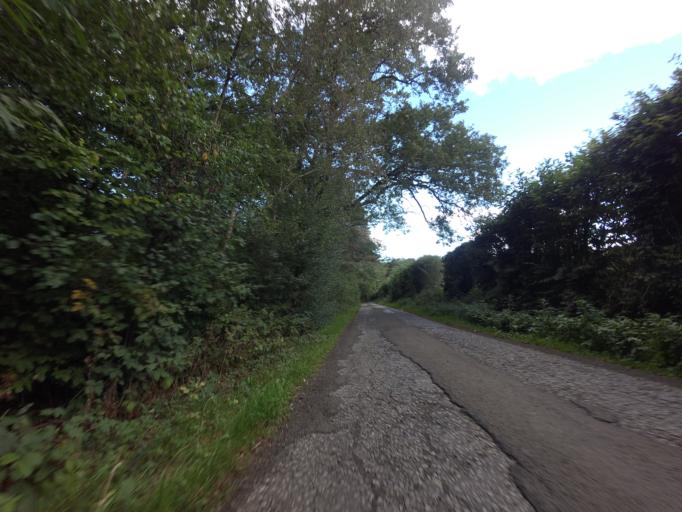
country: GB
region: England
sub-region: Kent
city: Marden
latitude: 51.1485
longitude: 0.4960
